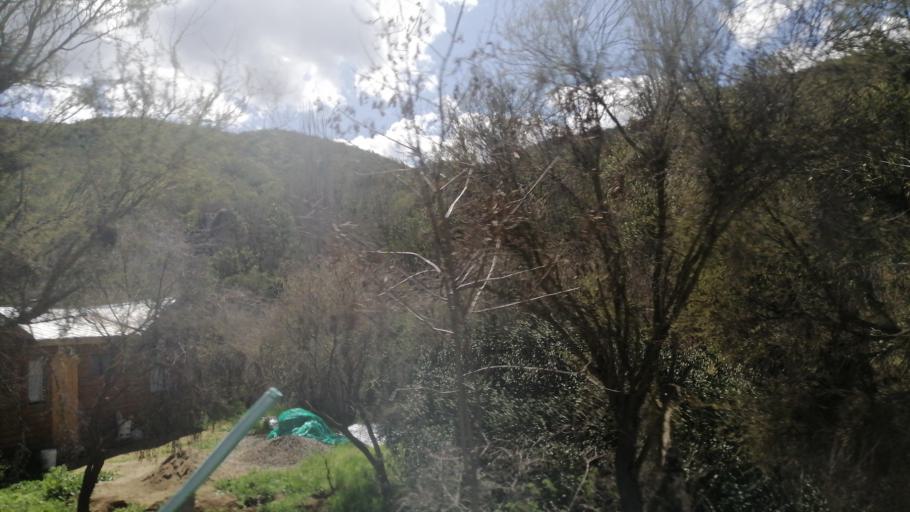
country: CL
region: Valparaiso
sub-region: Provincia de Marga Marga
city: Limache
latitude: -33.1793
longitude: -71.1822
